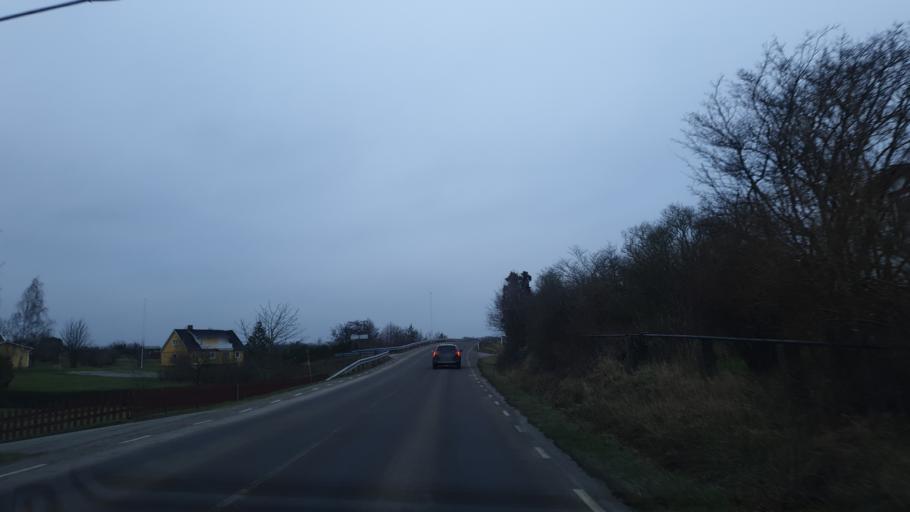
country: SE
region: Blekinge
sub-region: Karlskrona Kommun
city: Sturko
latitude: 56.1168
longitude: 15.7307
